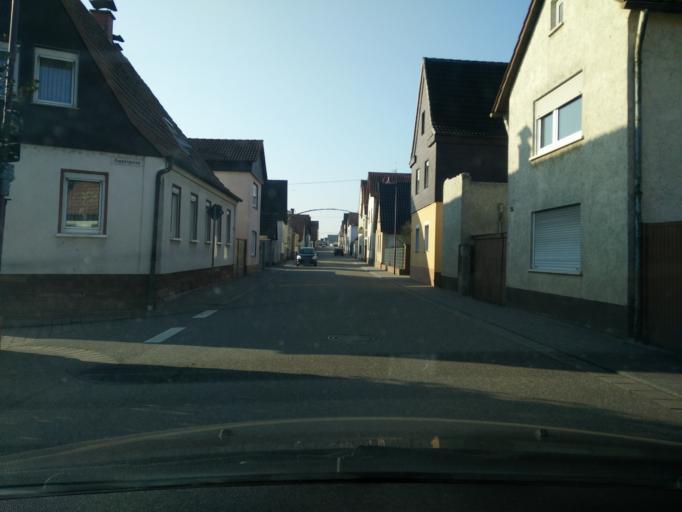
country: DE
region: Rheinland-Pfalz
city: Steinweiler
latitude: 49.1212
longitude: 8.1416
